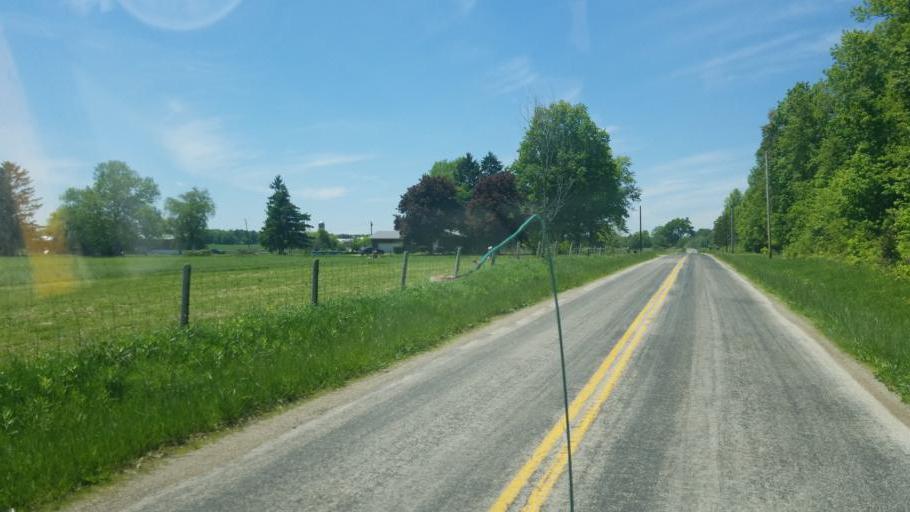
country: US
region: Ohio
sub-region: Huron County
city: New London
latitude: 40.9678
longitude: -82.4112
